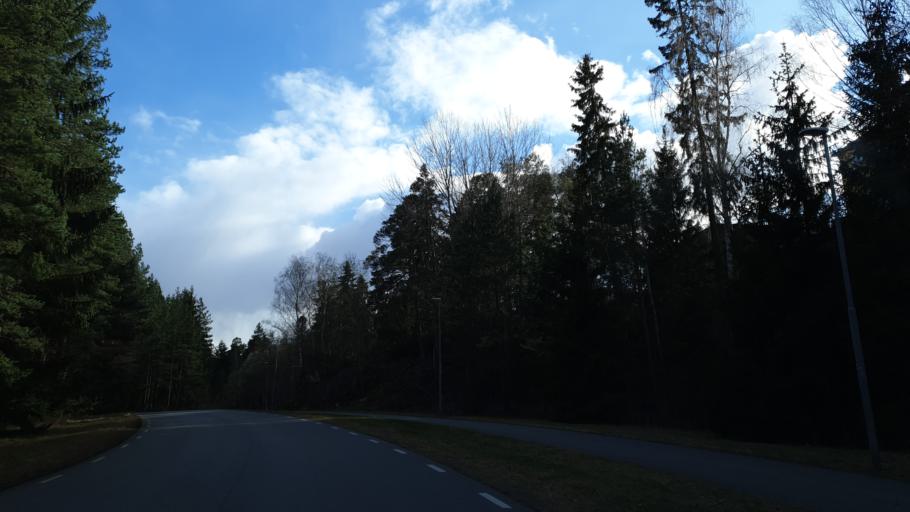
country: SE
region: Stockholm
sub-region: Lidingo
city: Lidingoe
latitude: 59.3867
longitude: 18.1192
